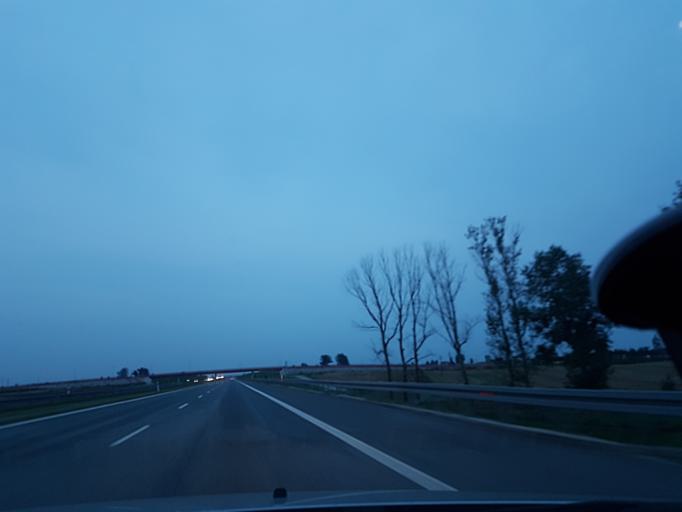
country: PL
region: Lodz Voivodeship
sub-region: Powiat kutnowski
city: Krzyzanow
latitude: 52.1728
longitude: 19.4852
